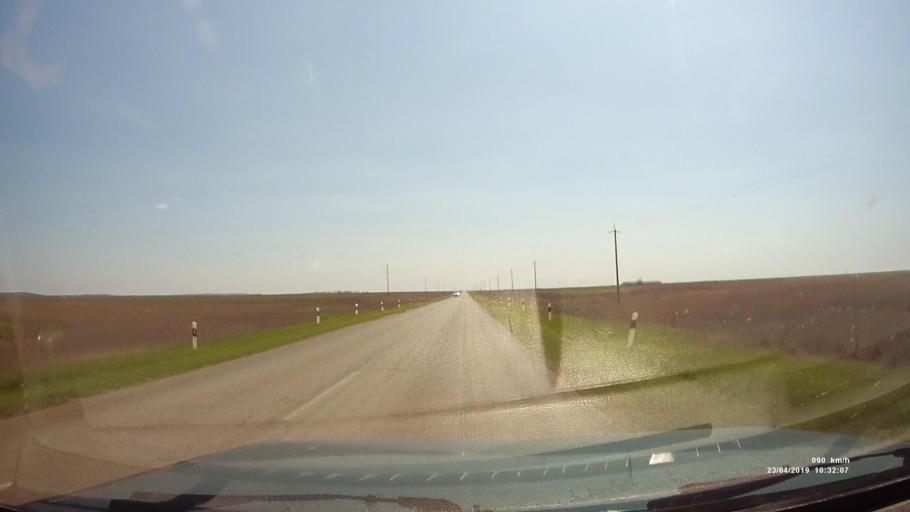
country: RU
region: Kalmykiya
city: Yashalta
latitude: 46.5822
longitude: 42.5724
